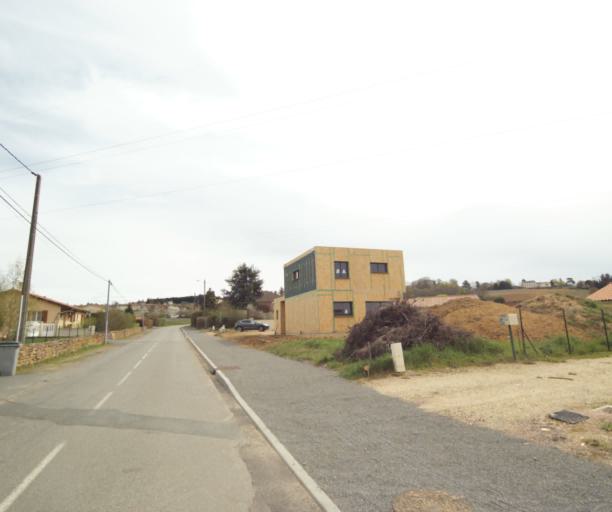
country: FR
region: Bourgogne
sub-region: Departement de Saone-et-Loire
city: Charnay-les-Macon
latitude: 46.3119
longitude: 4.7755
